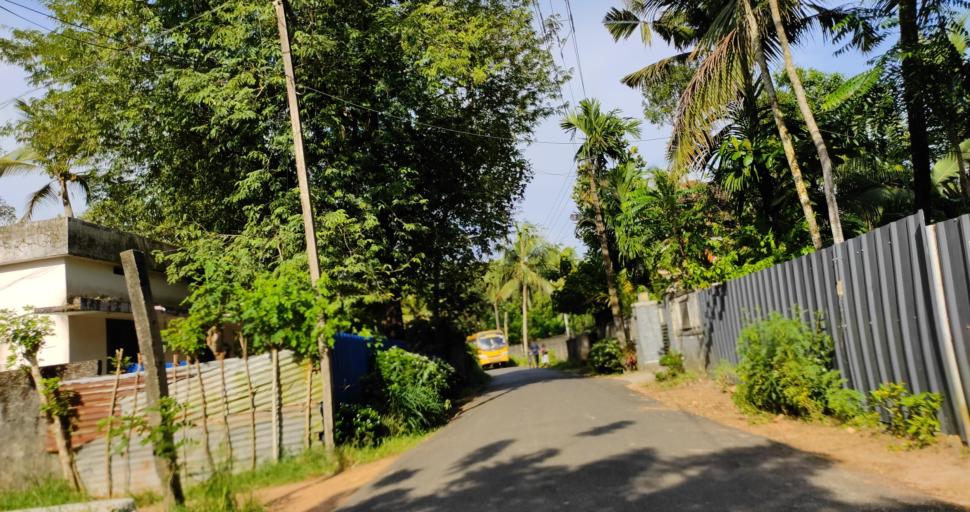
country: IN
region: Kerala
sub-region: Alappuzha
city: Shertallai
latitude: 9.6009
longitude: 76.3310
